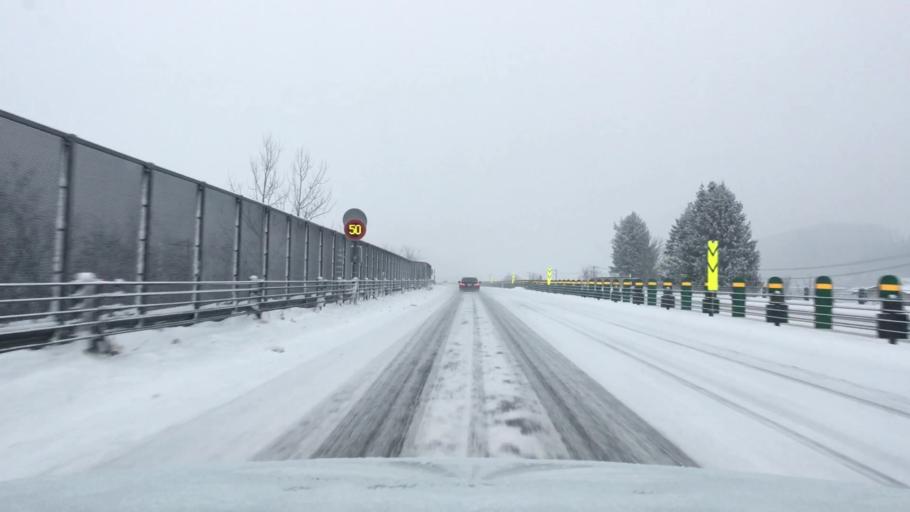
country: JP
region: Akita
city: Hanawa
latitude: 40.2772
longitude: 140.7615
